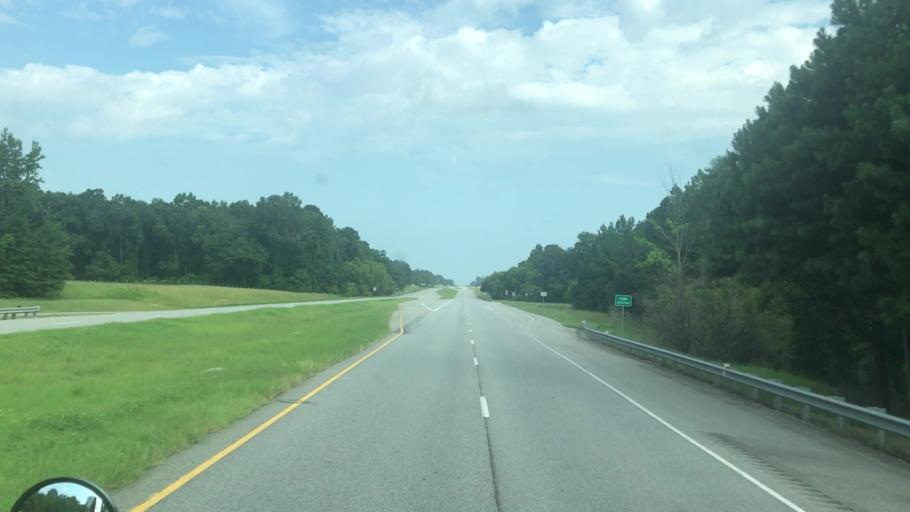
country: US
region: Georgia
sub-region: Early County
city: Blakely
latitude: 31.2987
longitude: -84.8578
